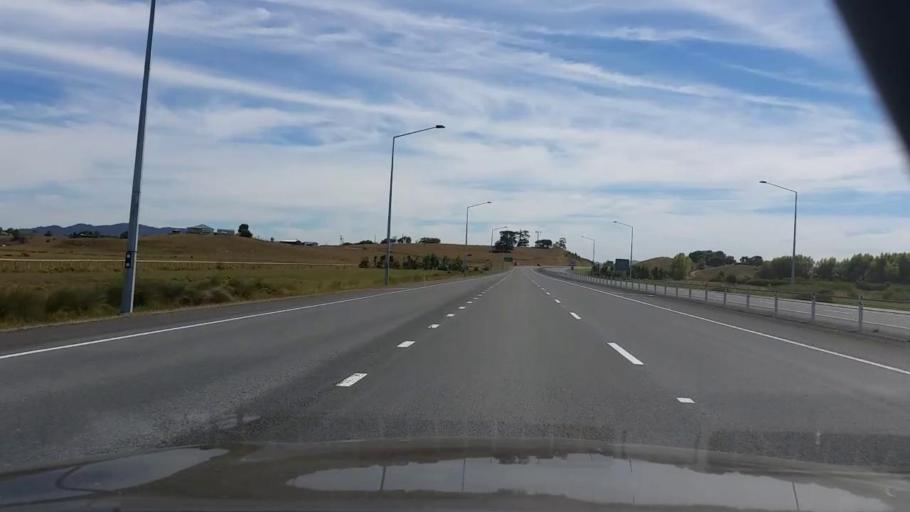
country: NZ
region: Waikato
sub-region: Waikato District
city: Ngaruawahia
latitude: -37.7297
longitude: 175.2087
